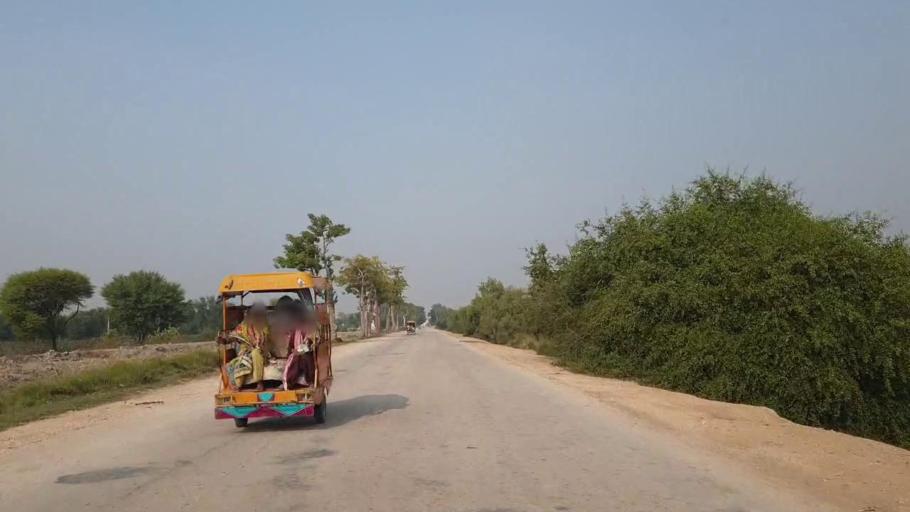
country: PK
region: Sindh
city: Bhan
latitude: 26.5831
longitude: 67.7288
